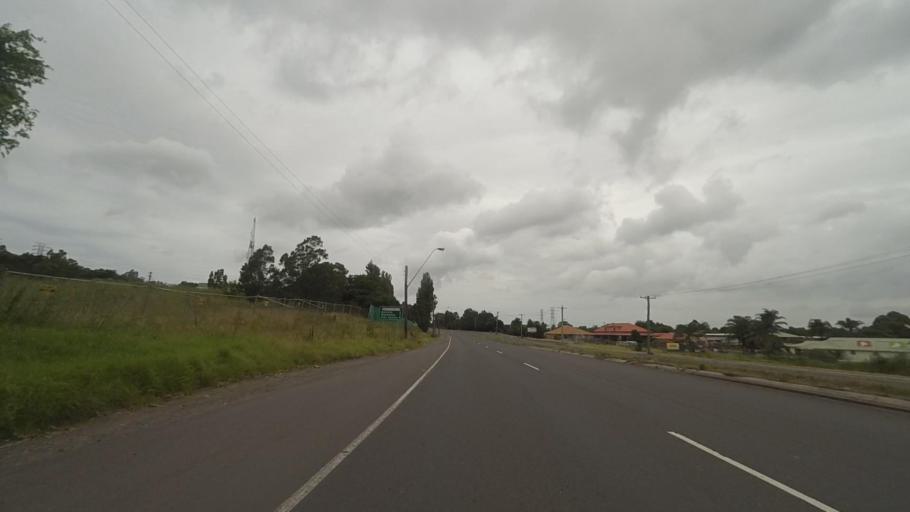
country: AU
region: New South Wales
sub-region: Wollongong
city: Berkeley
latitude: -34.4699
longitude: 150.8275
